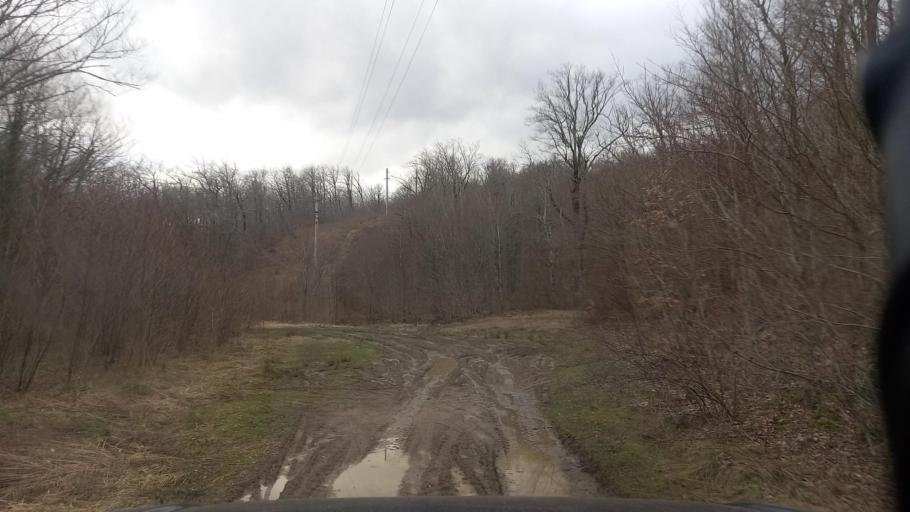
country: RU
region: Krasnodarskiy
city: Dzhubga
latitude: 44.4881
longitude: 38.7703
